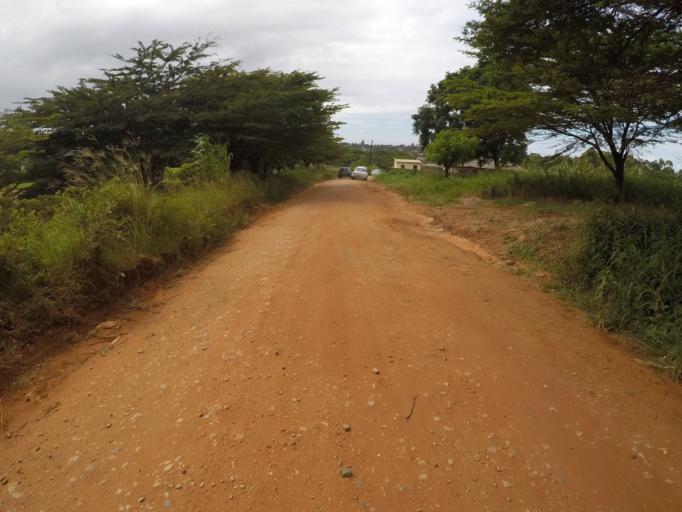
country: ZA
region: KwaZulu-Natal
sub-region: uThungulu District Municipality
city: eSikhawini
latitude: -28.8561
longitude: 31.9150
